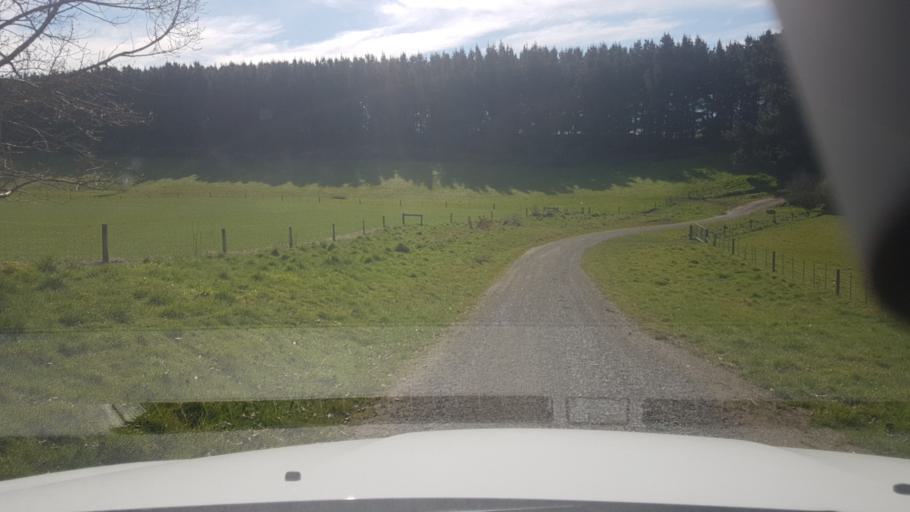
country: NZ
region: Canterbury
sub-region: Timaru District
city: Pleasant Point
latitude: -44.1972
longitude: 171.1876
